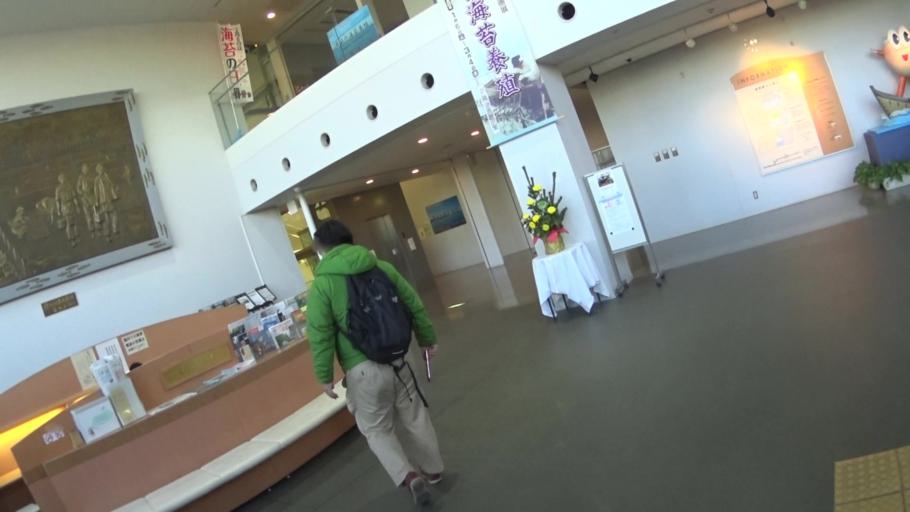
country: JP
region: Tokyo
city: Urayasu
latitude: 35.6552
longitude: 139.9015
